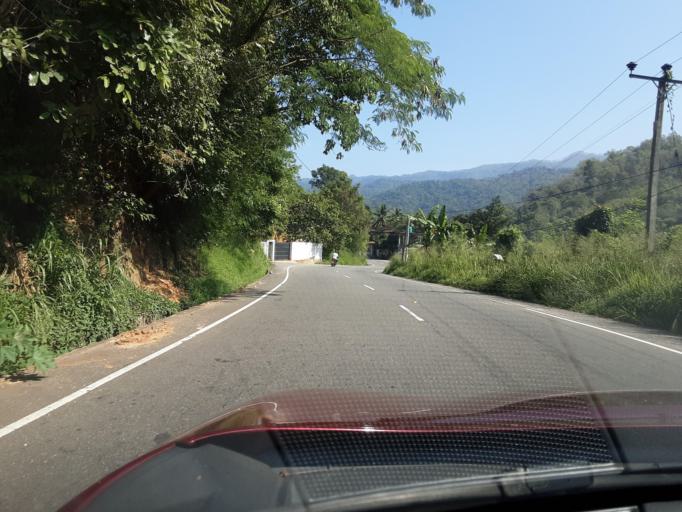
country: LK
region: Uva
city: Badulla
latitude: 7.0365
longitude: 81.0589
